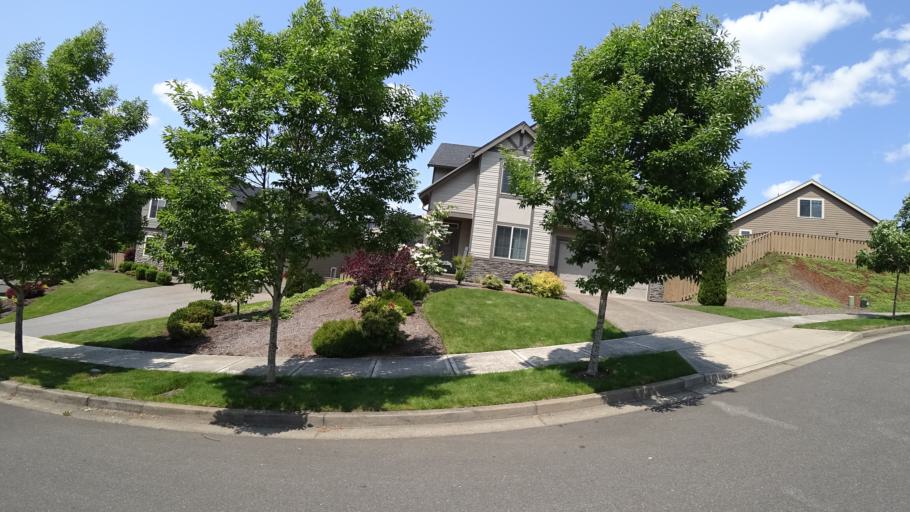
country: US
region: Oregon
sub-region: Clackamas County
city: Happy Valley
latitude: 45.4445
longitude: -122.5492
